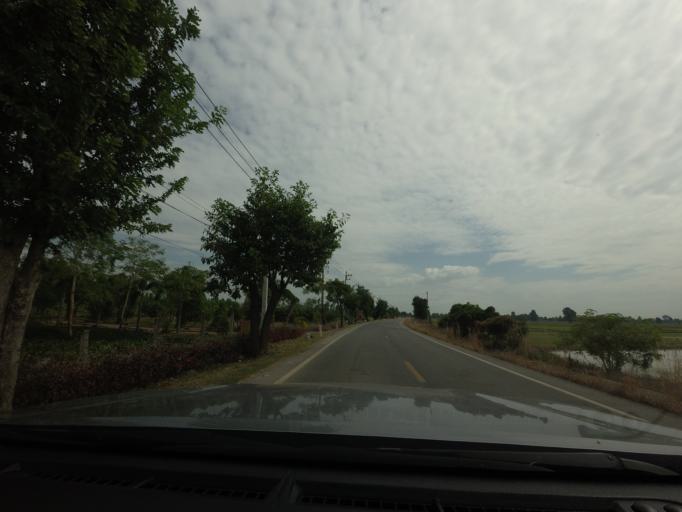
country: TH
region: Phitsanulok
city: Phitsanulok
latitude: 16.7212
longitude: 100.3382
